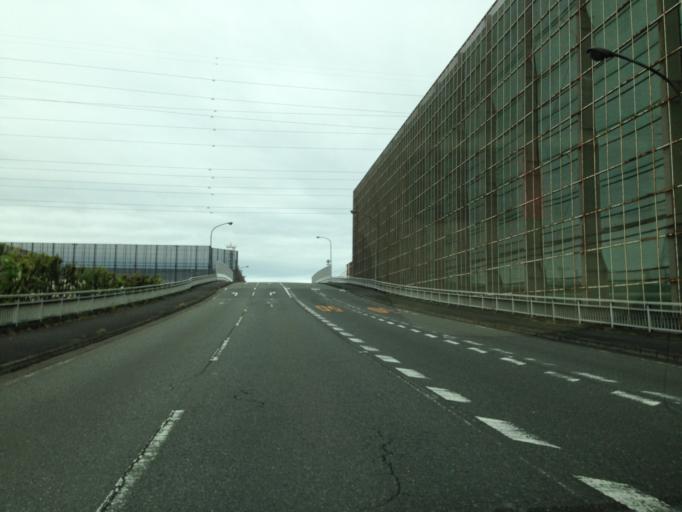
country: JP
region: Shizuoka
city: Fuji
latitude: 35.1472
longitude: 138.6907
